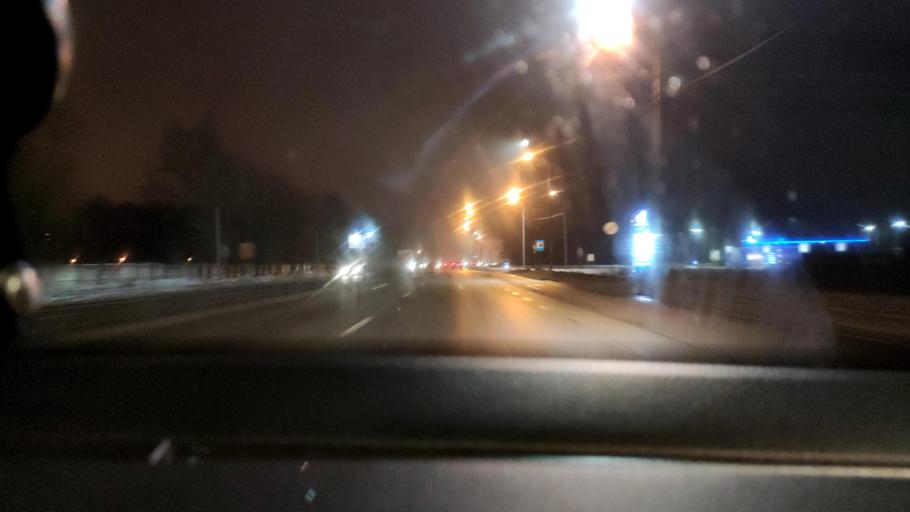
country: RU
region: Moskovskaya
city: Sergiyev Posad
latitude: 56.2511
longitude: 38.1231
